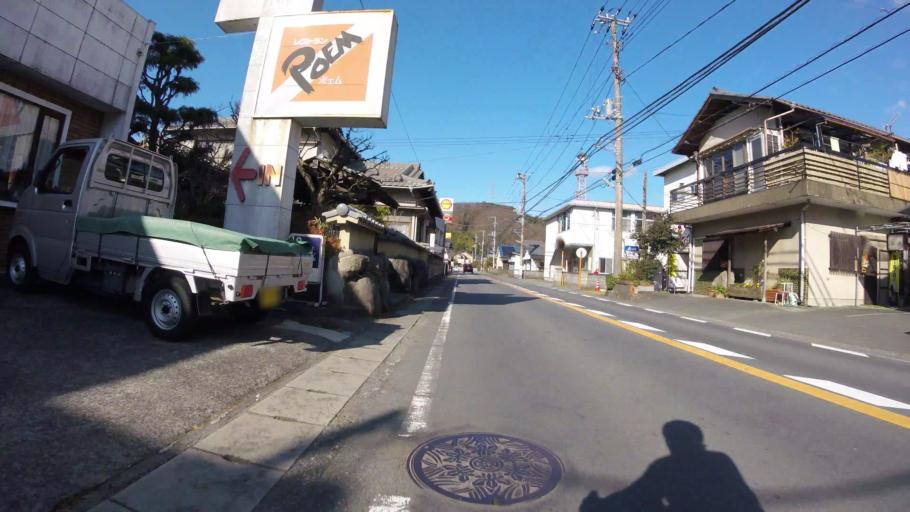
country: JP
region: Shizuoka
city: Ito
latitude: 34.9897
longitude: 138.9533
